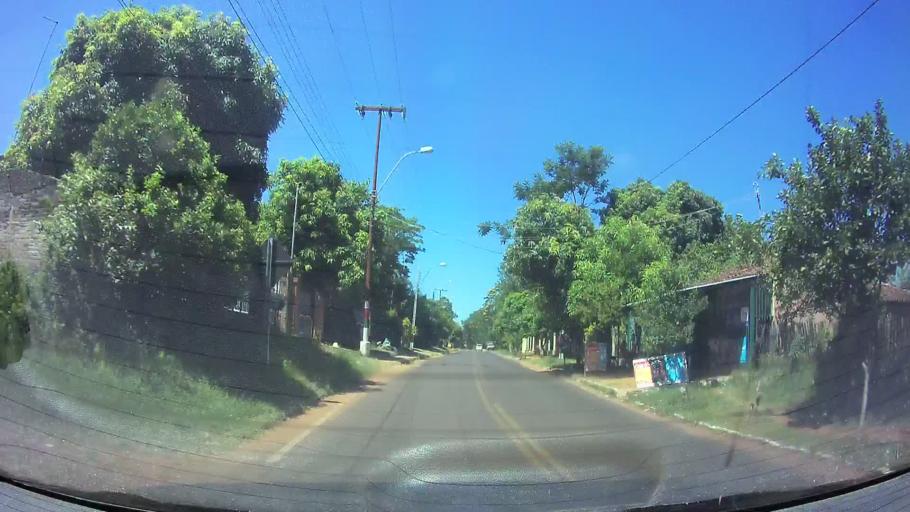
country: PY
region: Central
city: Aregua
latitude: -25.2955
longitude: -57.4146
